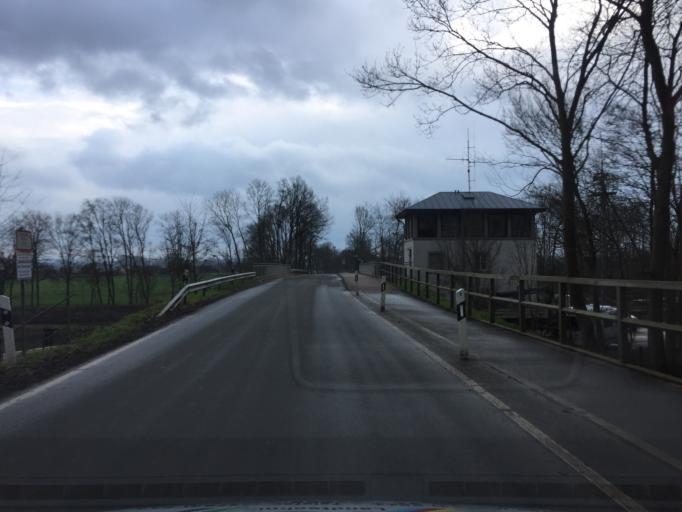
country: DE
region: Lower Saxony
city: Stolzenau
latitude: 52.4952
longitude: 9.0598
